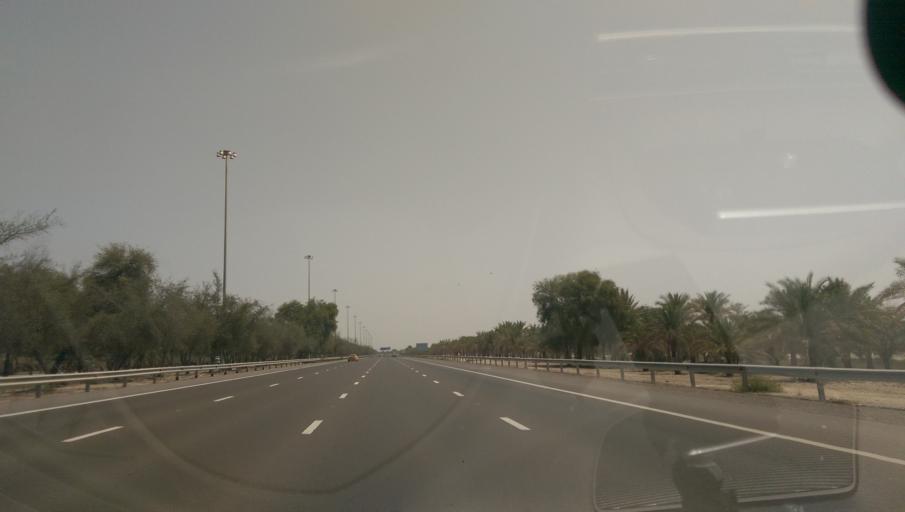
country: AE
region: Abu Dhabi
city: Abu Dhabi
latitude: 24.5098
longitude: 54.6865
